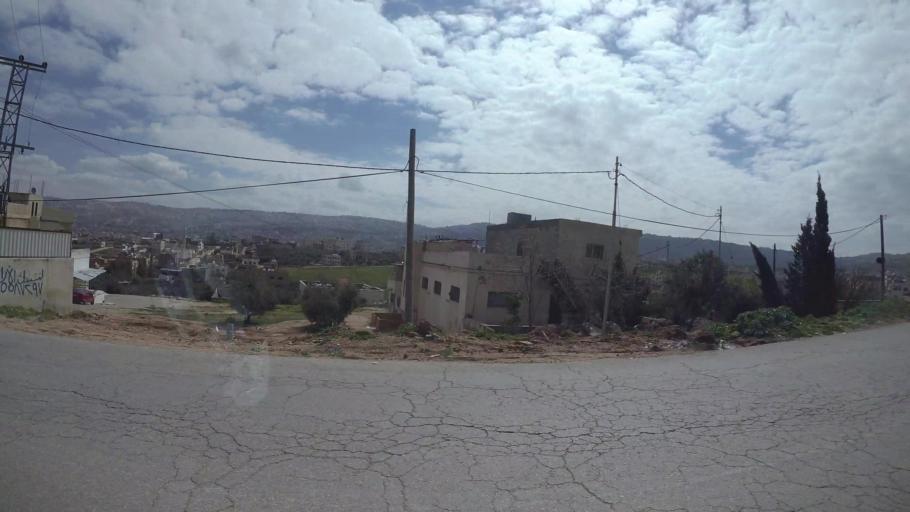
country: JO
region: Amman
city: Al Jubayhah
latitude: 32.0635
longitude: 35.8092
